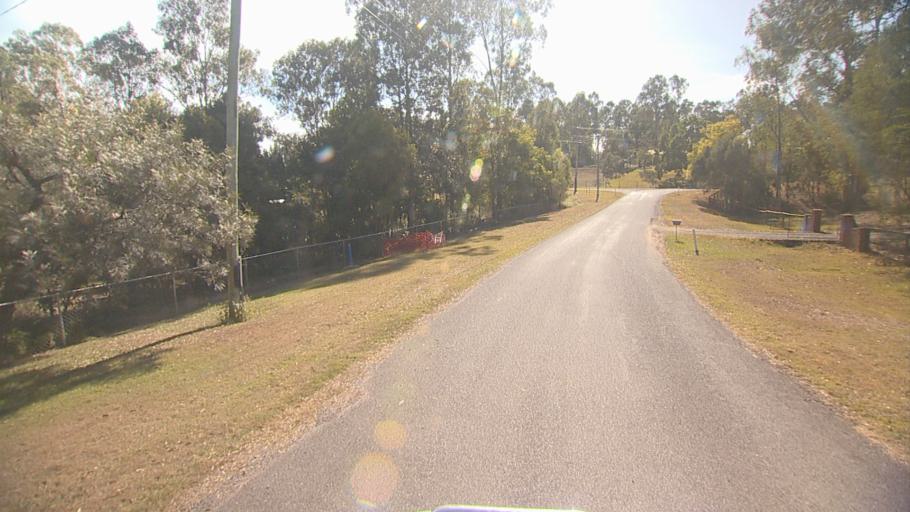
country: AU
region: Queensland
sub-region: Logan
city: Cedar Vale
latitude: -27.8532
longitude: 152.9894
